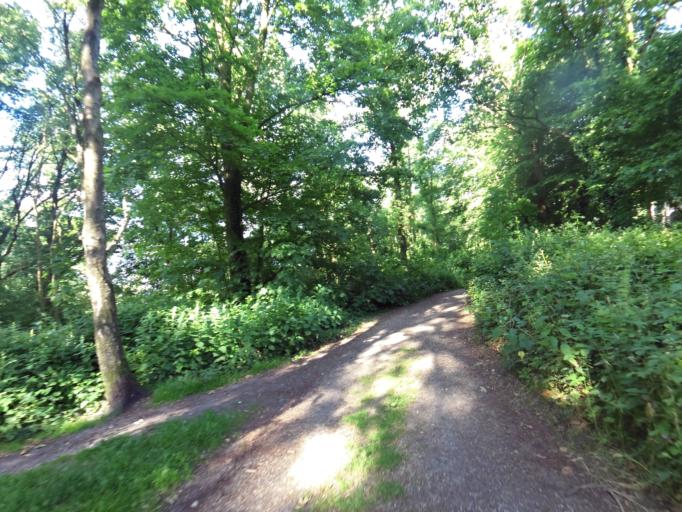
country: NL
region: Limburg
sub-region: Gemeente Heerlen
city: Heerlen
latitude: 50.9126
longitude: 6.0204
